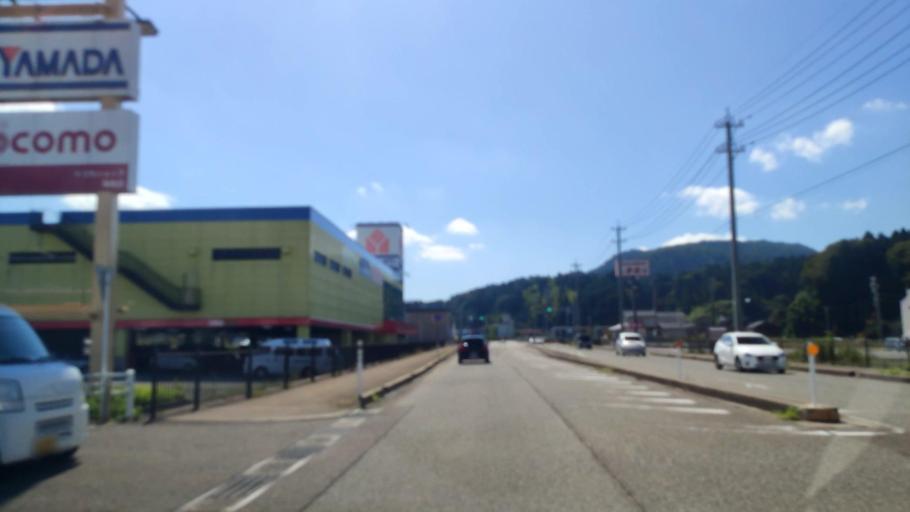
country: JP
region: Ishikawa
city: Nanao
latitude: 37.3863
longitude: 136.9026
